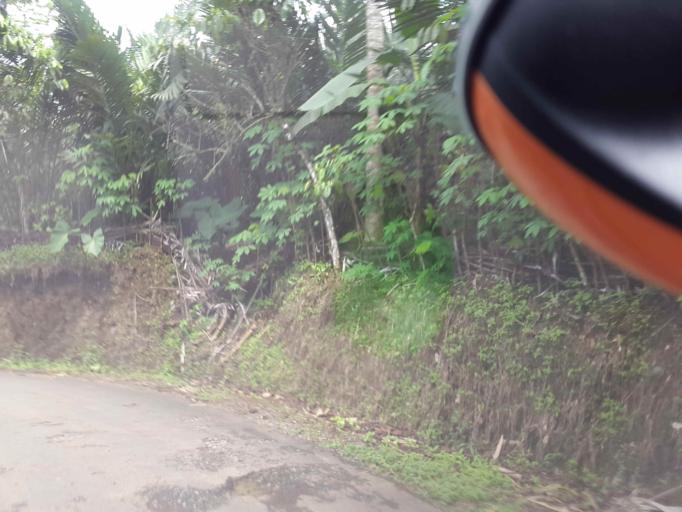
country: ID
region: Central Java
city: Wonosobo
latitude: -7.3363
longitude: 109.6851
